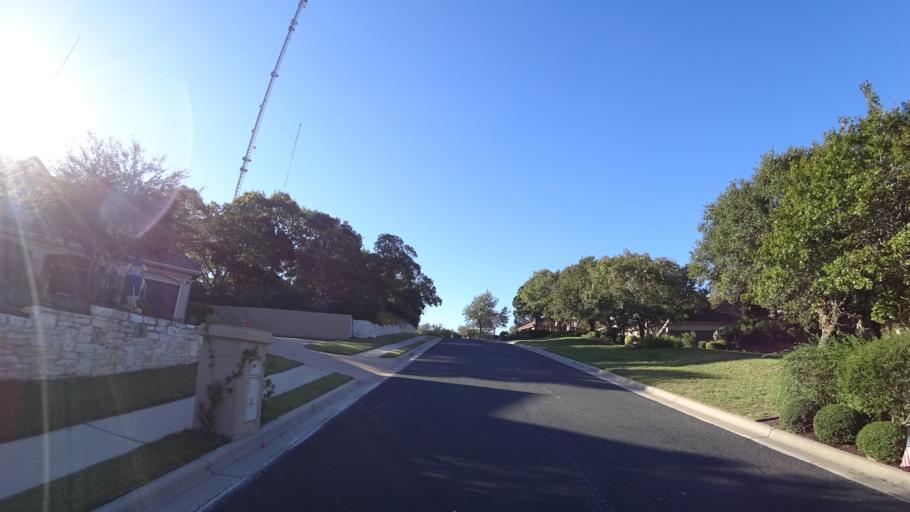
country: US
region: Texas
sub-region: Travis County
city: West Lake Hills
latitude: 30.3241
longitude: -97.8051
